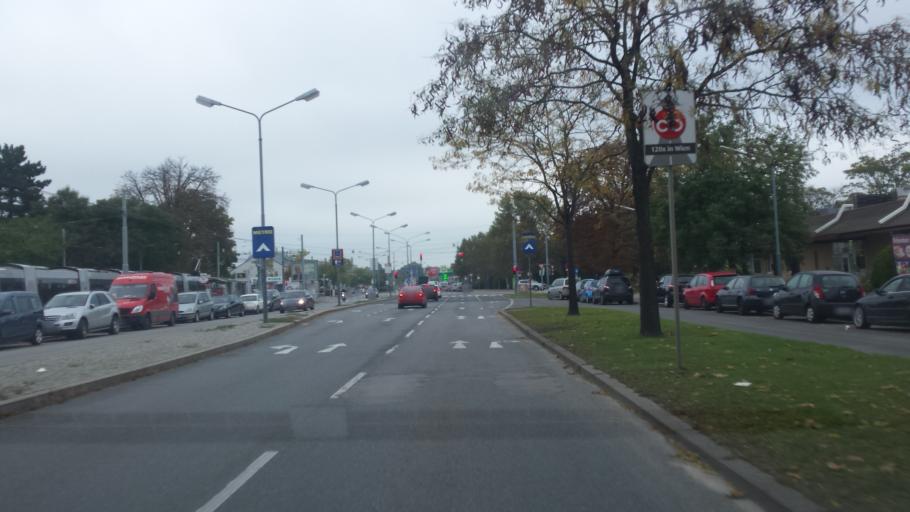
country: AT
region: Lower Austria
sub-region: Politischer Bezirk Wien-Umgebung
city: Schwechat
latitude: 48.1588
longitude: 16.4703
